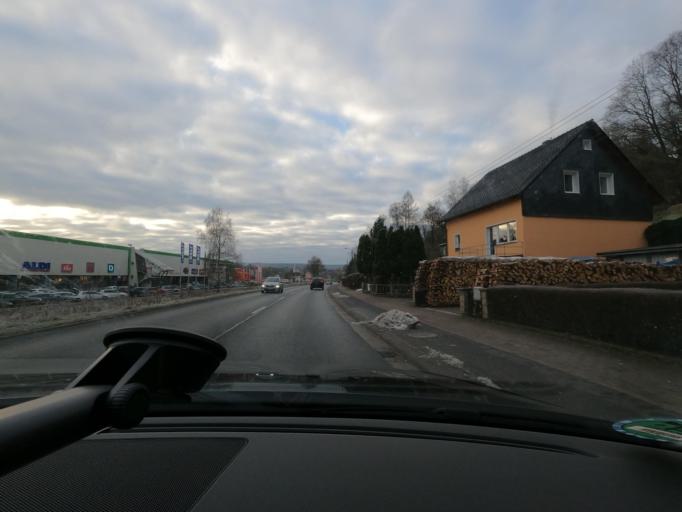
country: DE
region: Thuringia
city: Schleusingen
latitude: 50.5176
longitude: 10.7539
